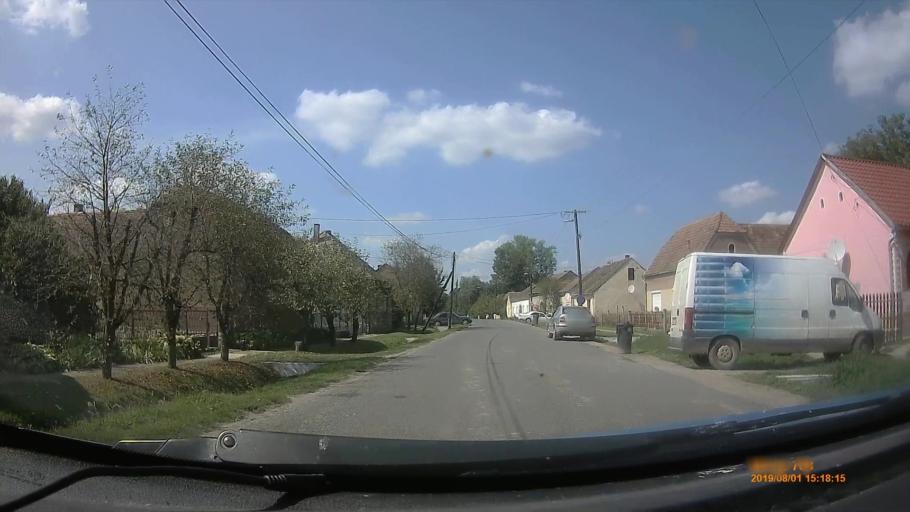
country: HU
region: Baranya
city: Sellye
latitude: 45.8477
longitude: 17.8165
